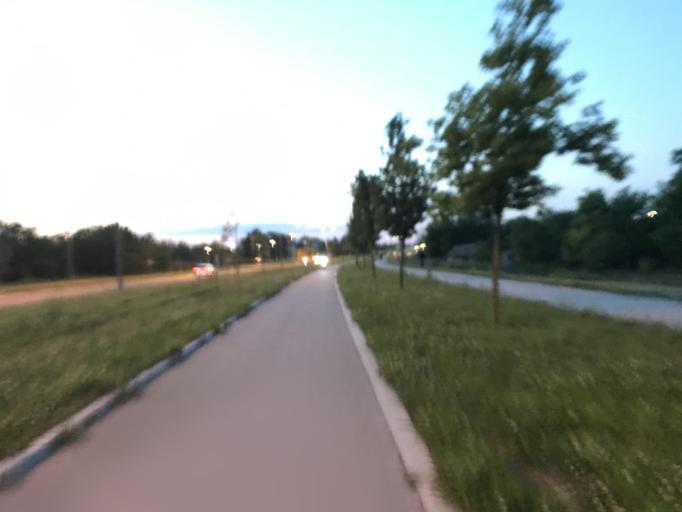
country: RS
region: Autonomna Pokrajina Vojvodina
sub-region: Juznobacki Okrug
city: Novi Sad
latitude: 45.2731
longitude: 19.8009
